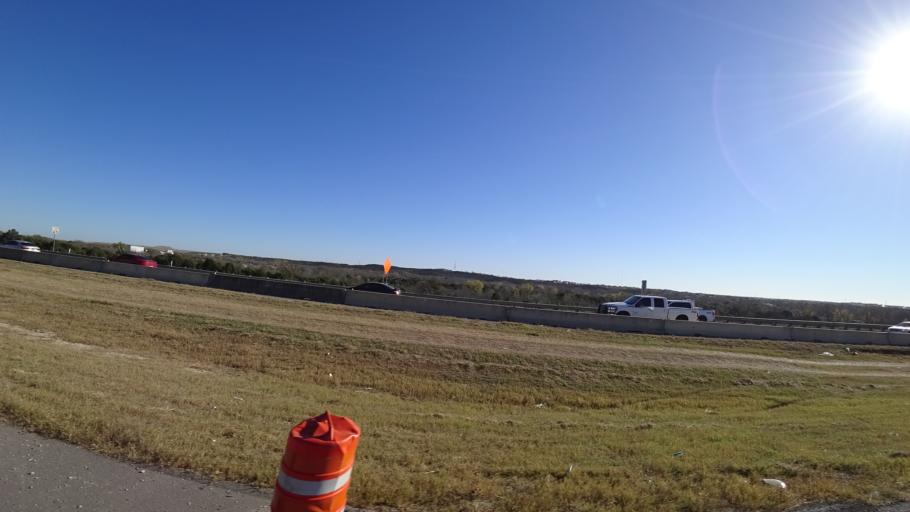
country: US
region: Texas
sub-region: Travis County
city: Austin
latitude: 30.3076
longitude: -97.6612
